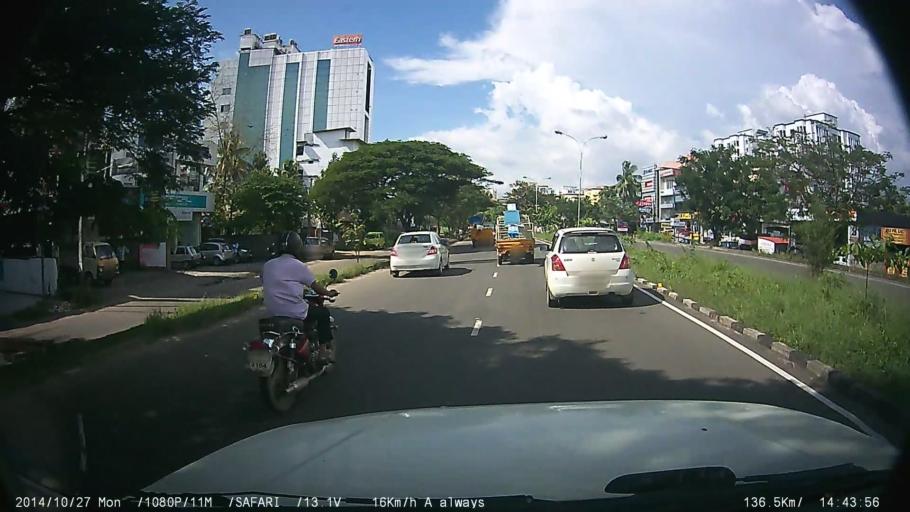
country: IN
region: Kerala
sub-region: Ernakulam
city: Elur
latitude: 10.0192
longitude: 76.3107
